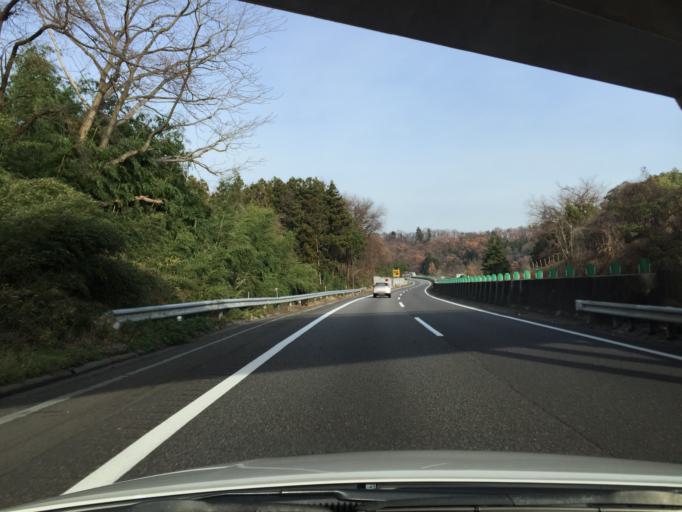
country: JP
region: Fukushima
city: Nihommatsu
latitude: 37.6208
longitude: 140.4257
